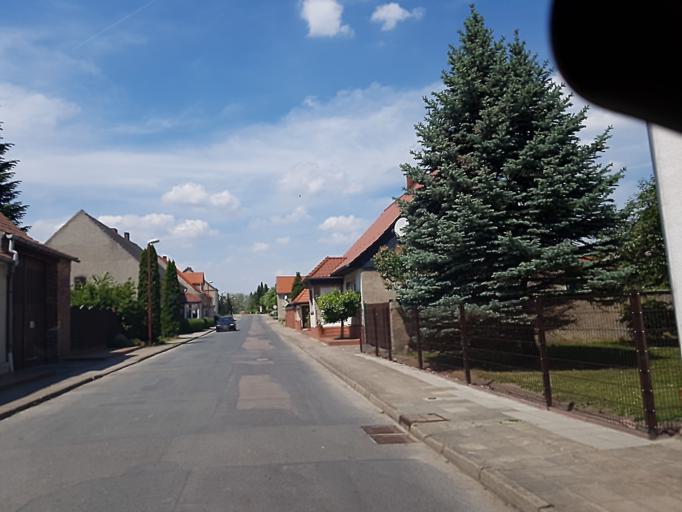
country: DE
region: Brandenburg
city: Gorzke
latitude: 52.1117
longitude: 12.3695
